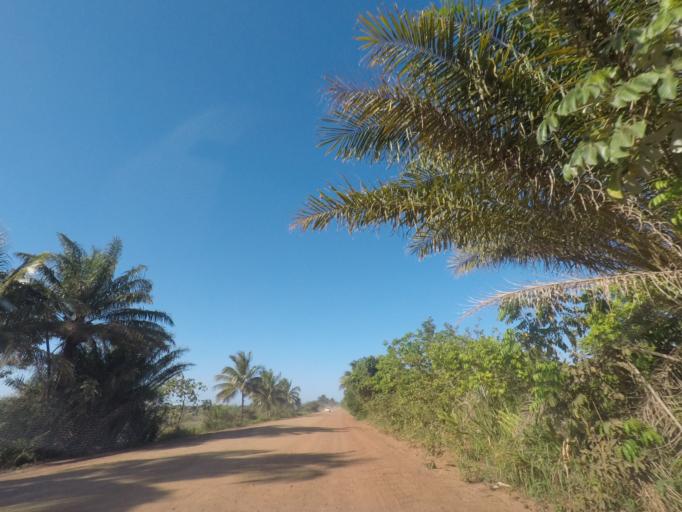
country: BR
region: Bahia
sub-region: Marau
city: Marau
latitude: -14.0573
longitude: -38.9564
